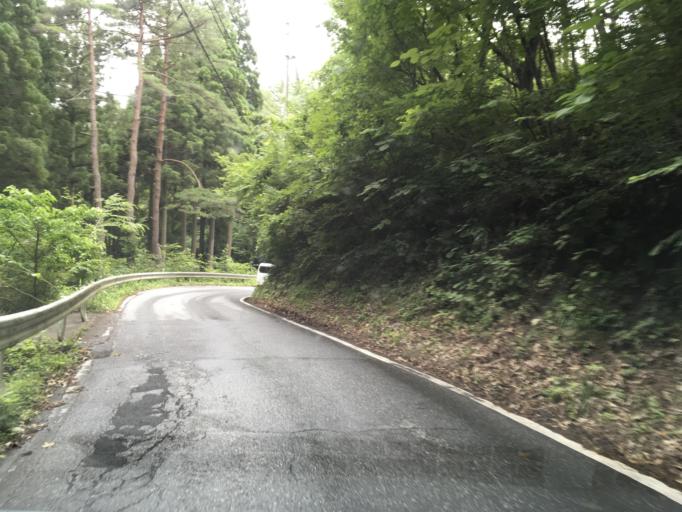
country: JP
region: Iwate
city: Ofunato
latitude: 38.9177
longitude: 141.6071
